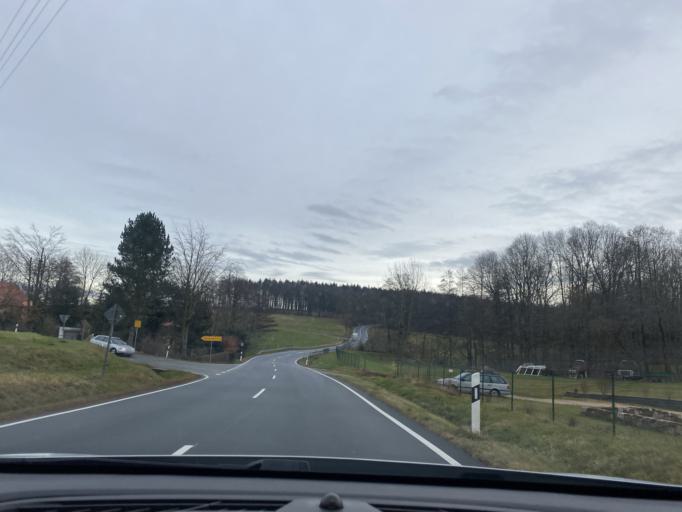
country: DE
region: Saxony
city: Reichenbach
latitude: 51.1170
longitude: 14.8345
